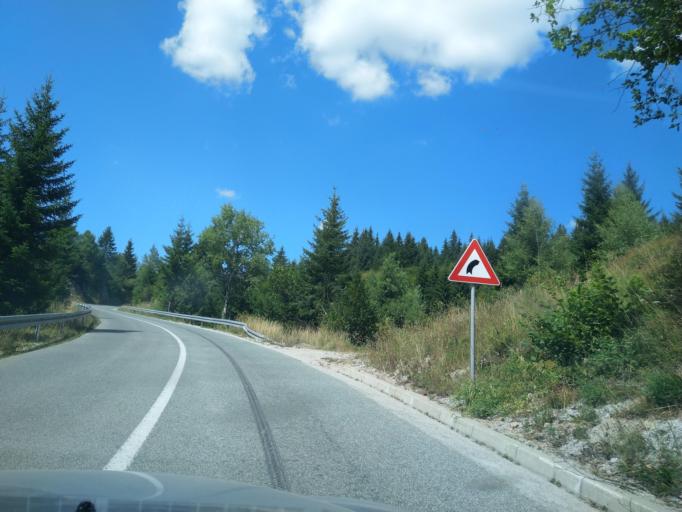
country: RS
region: Central Serbia
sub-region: Zlatiborski Okrug
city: Nova Varos
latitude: 43.4020
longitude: 19.8447
